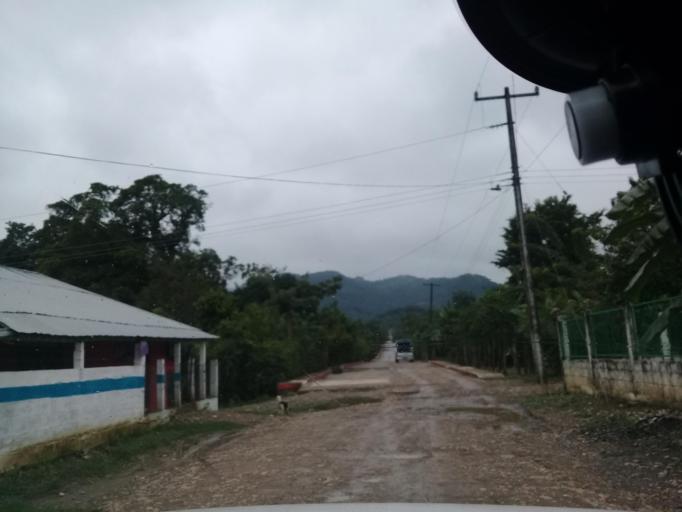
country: MX
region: Veracruz
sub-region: Chalma
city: San Pedro Coyutla
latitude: 21.2274
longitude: -98.4257
